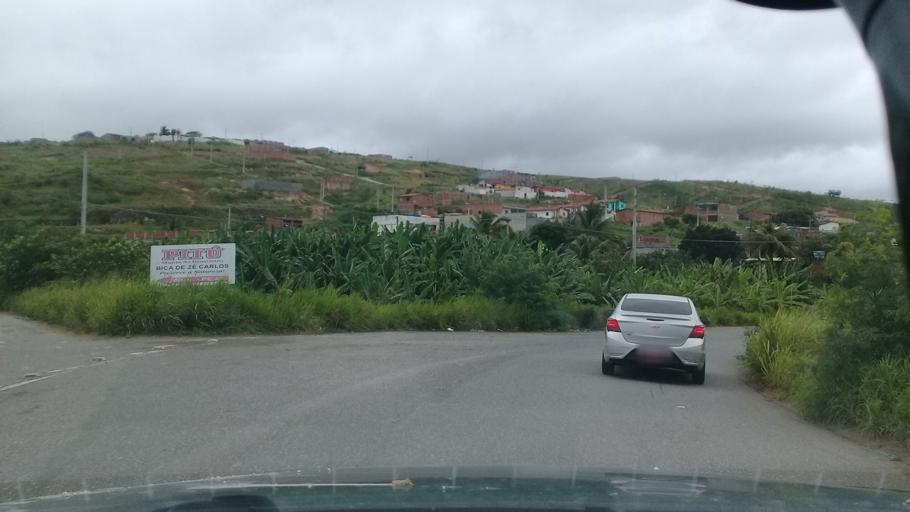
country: BR
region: Pernambuco
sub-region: Vitoria De Santo Antao
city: Vitoria de Santo Antao
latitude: -8.1300
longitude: -35.2825
